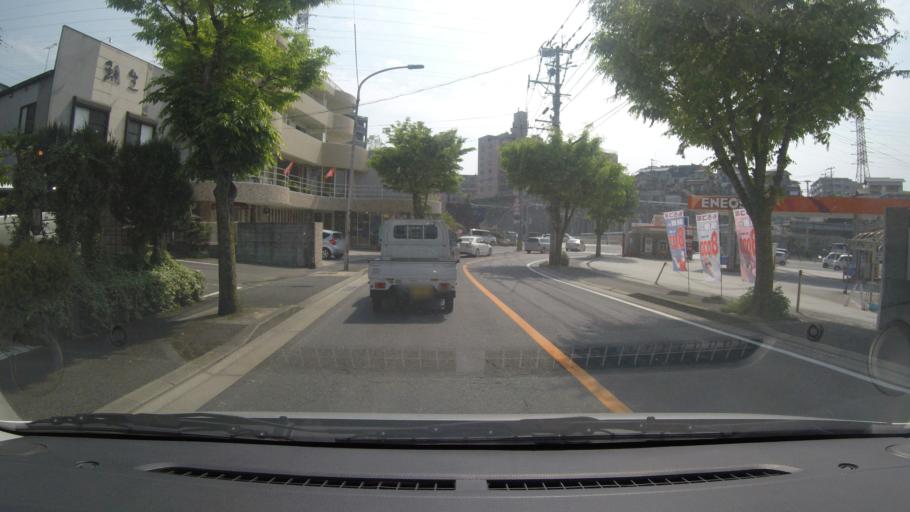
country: JP
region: Fukuoka
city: Fukuoka-shi
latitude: 33.6408
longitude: 130.4418
